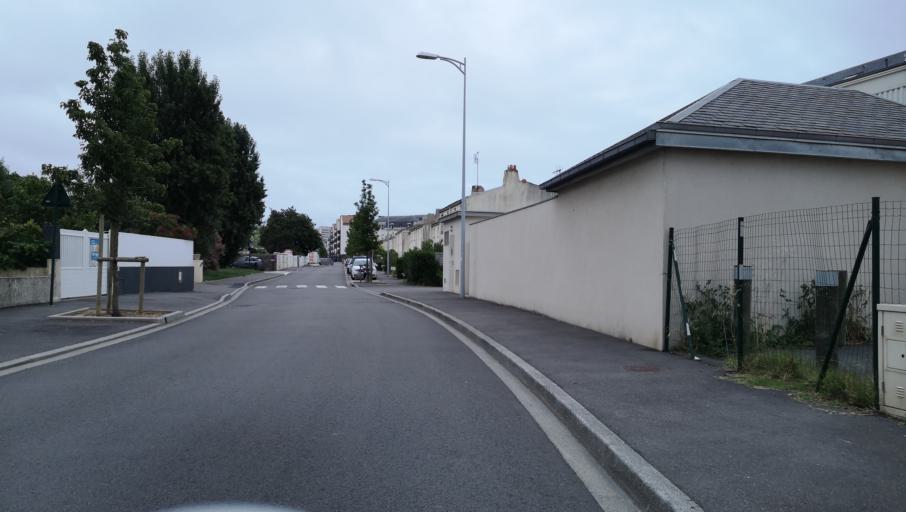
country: FR
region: Pays de la Loire
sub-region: Departement de la Vendee
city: Les Sables-d'Olonne
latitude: 46.5049
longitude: -1.7876
